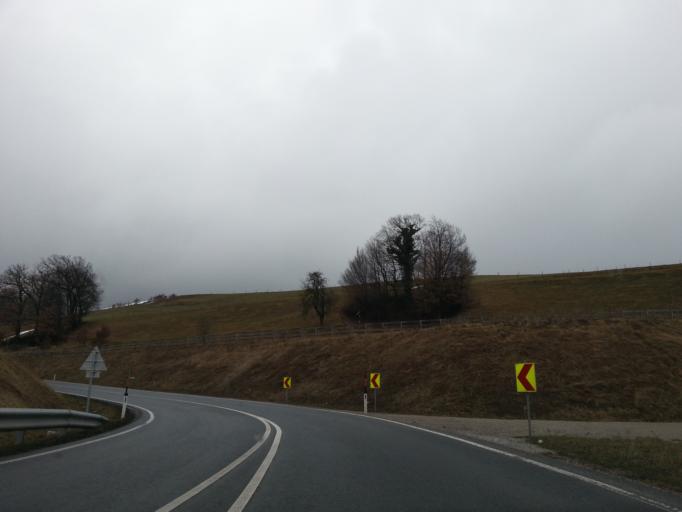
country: AT
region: Salzburg
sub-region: Politischer Bezirk Salzburg-Umgebung
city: Strasswalchen
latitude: 47.9851
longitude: 13.2533
